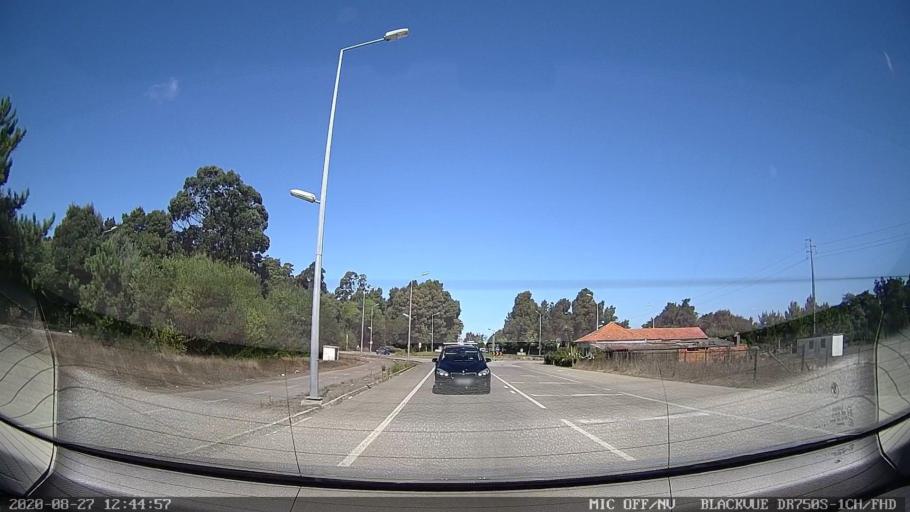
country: PT
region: Aveiro
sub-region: Ilhavo
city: Ilhavo
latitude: 40.6227
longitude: -8.6860
